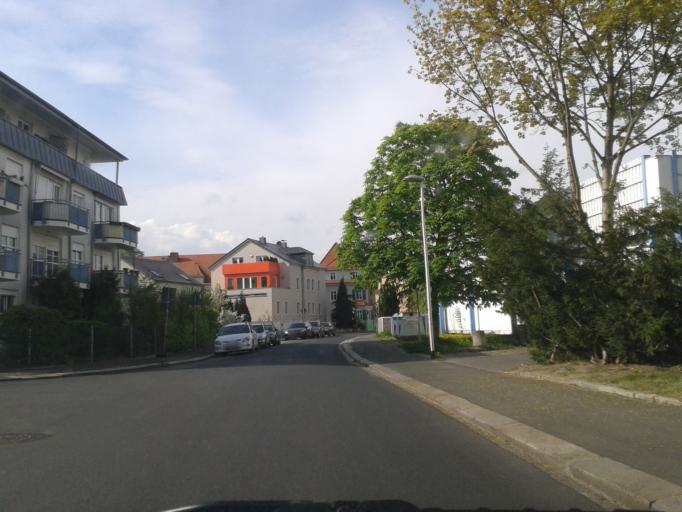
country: DE
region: Saxony
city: Radebeul
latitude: 51.0993
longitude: 13.6662
